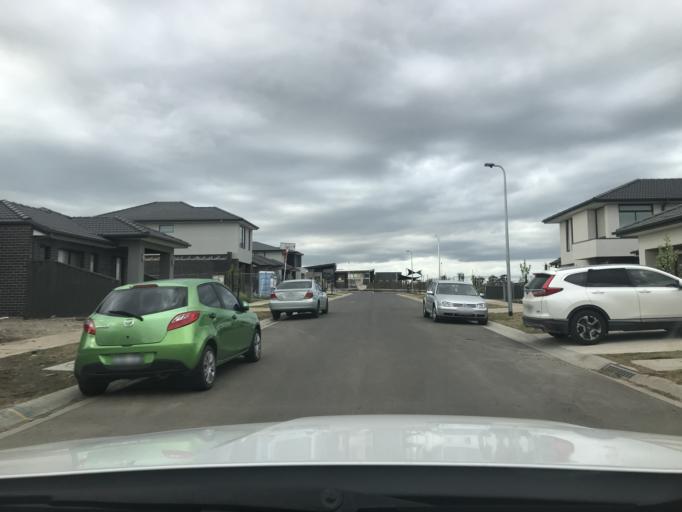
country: AU
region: Victoria
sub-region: Hume
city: Roxburgh Park
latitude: -37.5838
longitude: 144.8964
